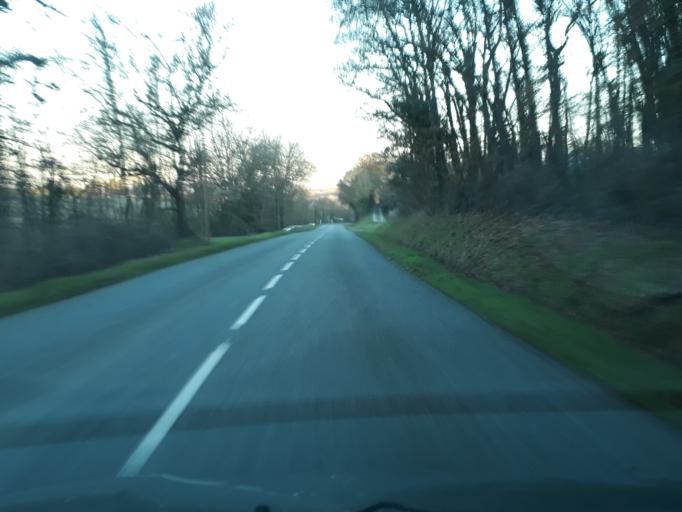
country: FR
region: Midi-Pyrenees
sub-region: Departement du Gers
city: Pavie
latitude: 43.6141
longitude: 0.6781
